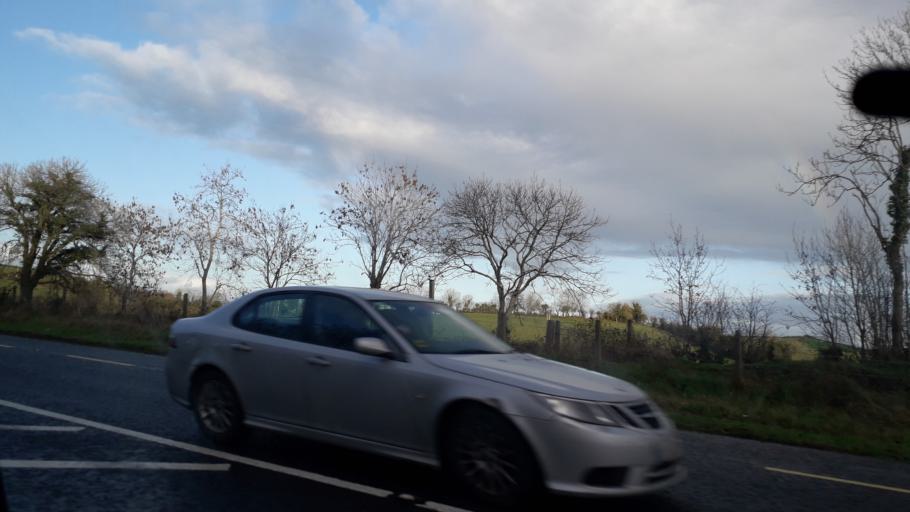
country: IE
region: Ulster
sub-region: County Monaghan
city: Castleblayney
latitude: 54.0608
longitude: -6.6969
